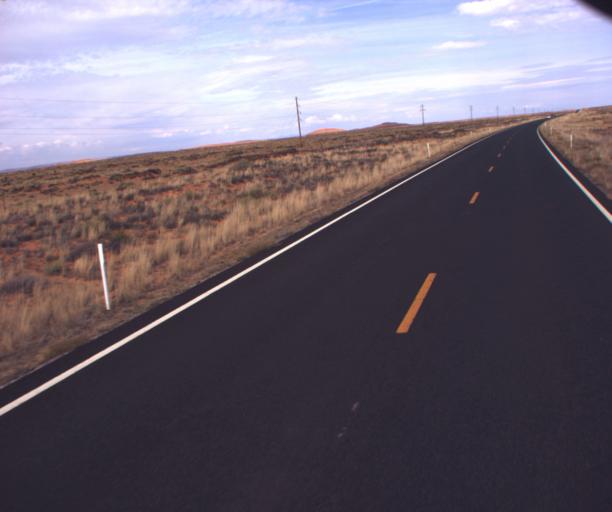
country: US
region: Arizona
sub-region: Apache County
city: Many Farms
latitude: 36.8361
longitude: -109.6427
